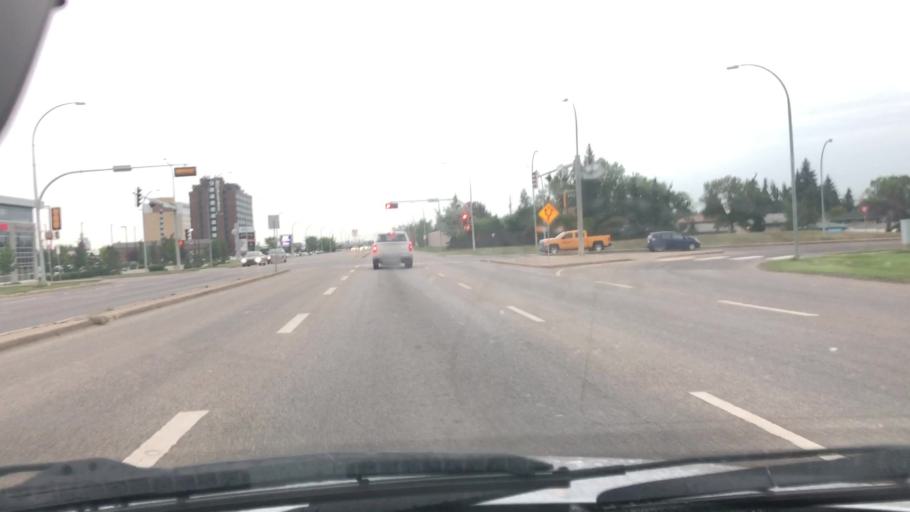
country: CA
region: Alberta
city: St. Albert
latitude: 53.5514
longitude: -113.6088
